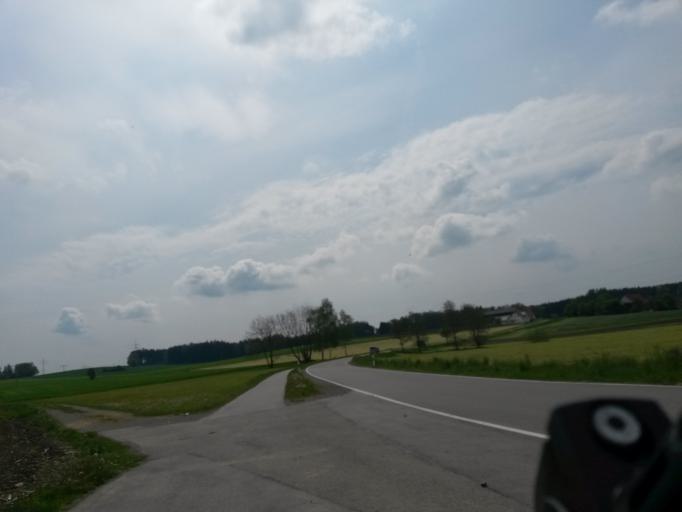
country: DE
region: Baden-Wuerttemberg
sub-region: Tuebingen Region
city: Bad Waldsee
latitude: 47.9600
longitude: 9.7334
